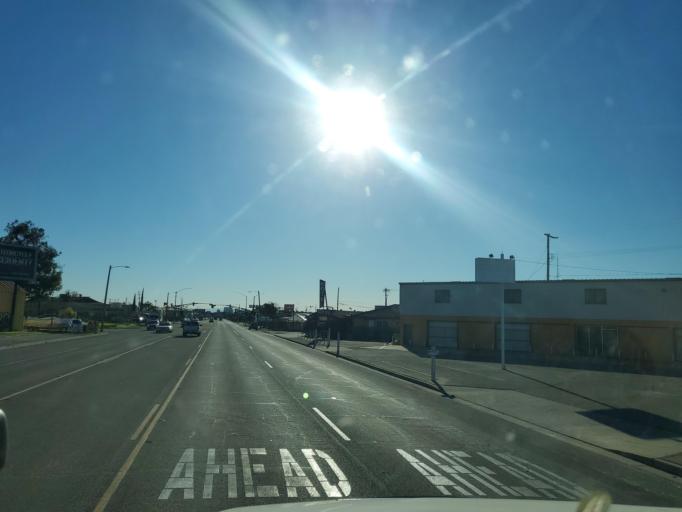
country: US
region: California
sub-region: San Joaquin County
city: August
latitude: 37.9850
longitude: -121.2703
